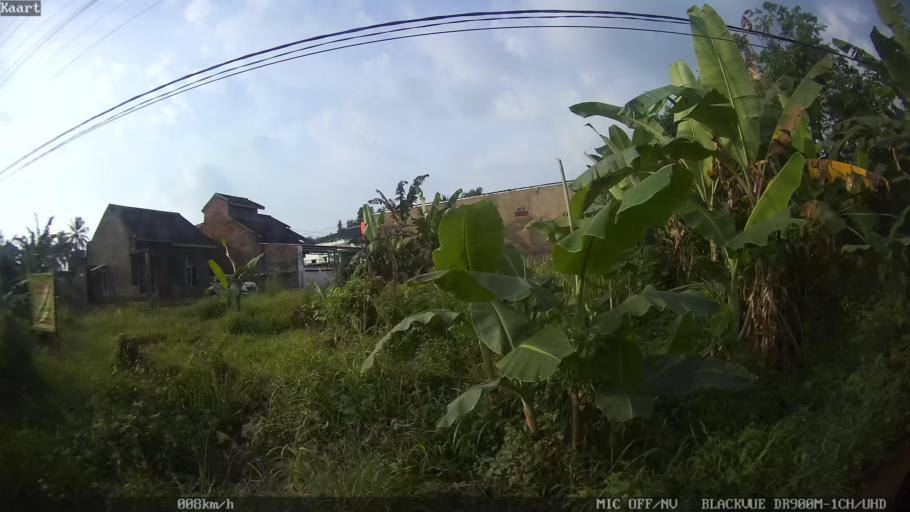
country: ID
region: Lampung
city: Kedaton
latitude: -5.3887
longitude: 105.3229
